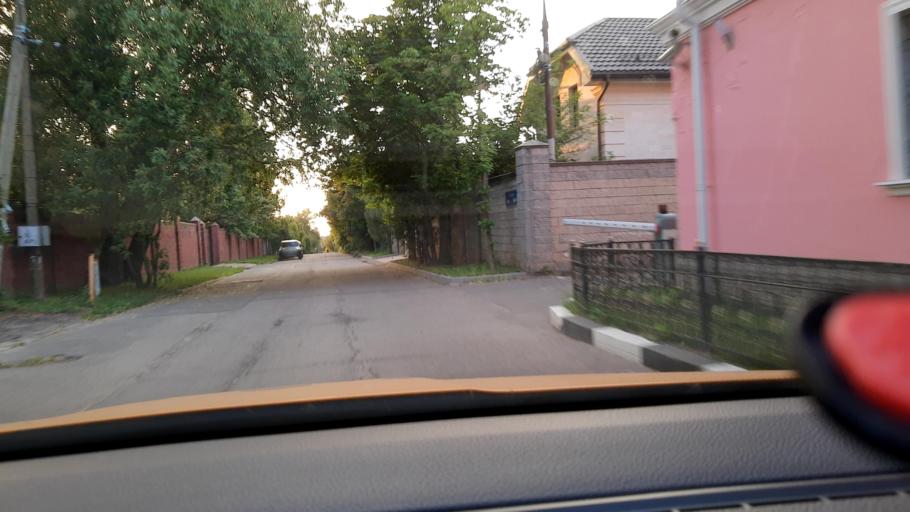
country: RU
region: Moskovskaya
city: Barvikha
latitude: 55.7253
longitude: 37.2968
